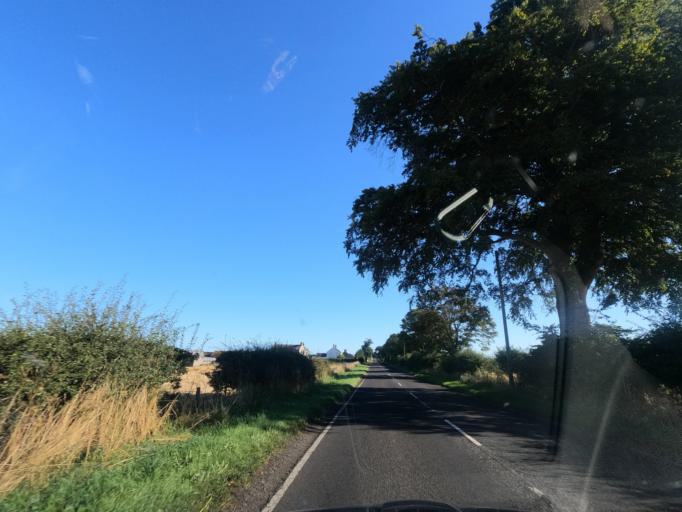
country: GB
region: England
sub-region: Northumberland
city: Ford
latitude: 55.7154
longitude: -2.1158
